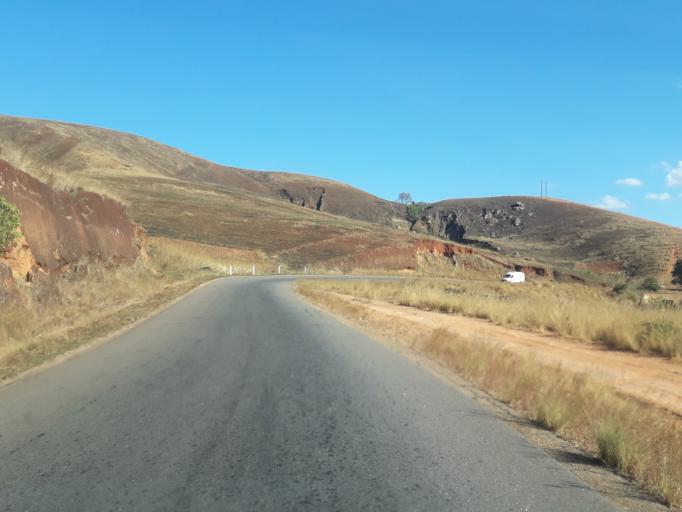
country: MG
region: Analamanga
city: Ankazobe
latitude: -17.7004
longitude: 46.9898
